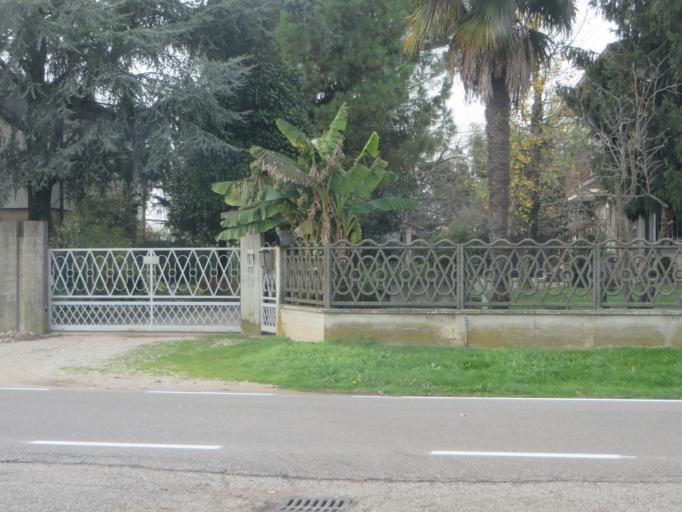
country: IT
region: Veneto
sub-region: Provincia di Verona
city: San Pietro di Morubio
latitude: 45.2518
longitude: 11.2341
